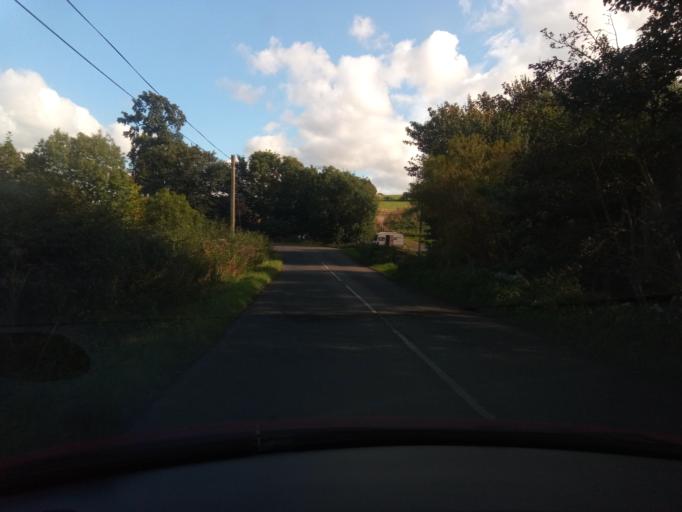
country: GB
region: Scotland
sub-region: The Scottish Borders
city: Coldstream
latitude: 55.5506
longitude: -2.3090
